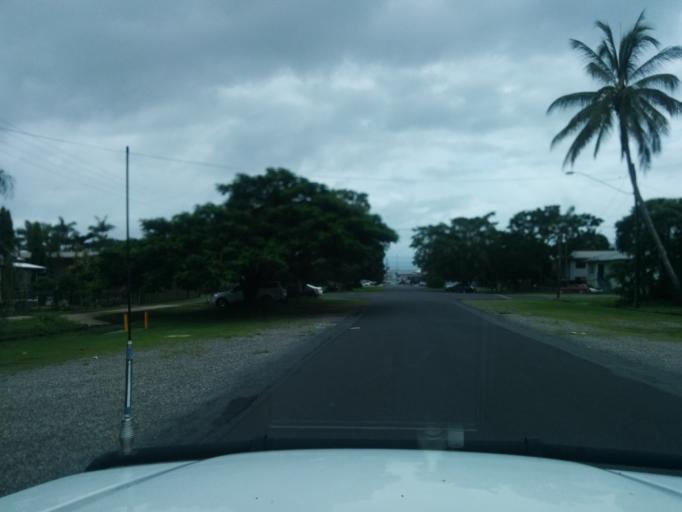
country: AU
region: Queensland
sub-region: Cairns
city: Cairns
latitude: -16.9308
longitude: 145.7559
